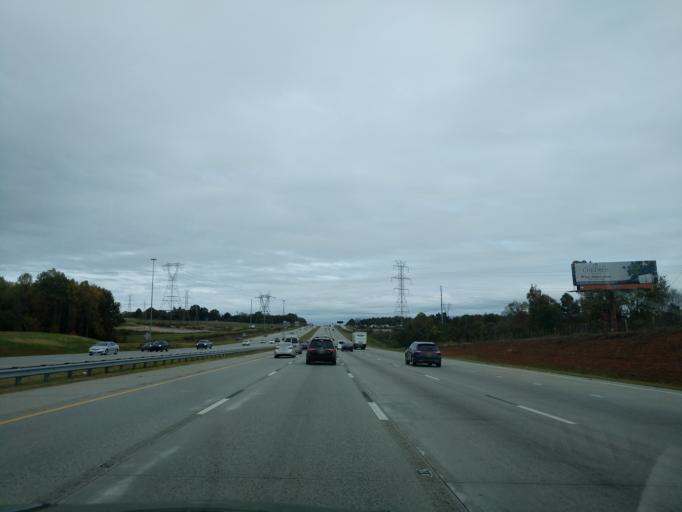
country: US
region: North Carolina
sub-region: Rowan County
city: Spencer
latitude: 35.7321
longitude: -80.3753
